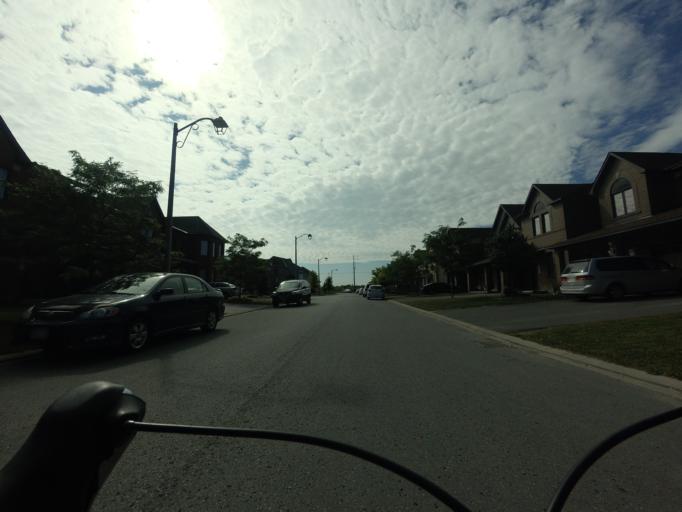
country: CA
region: Ontario
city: Bells Corners
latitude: 45.2685
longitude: -75.7328
